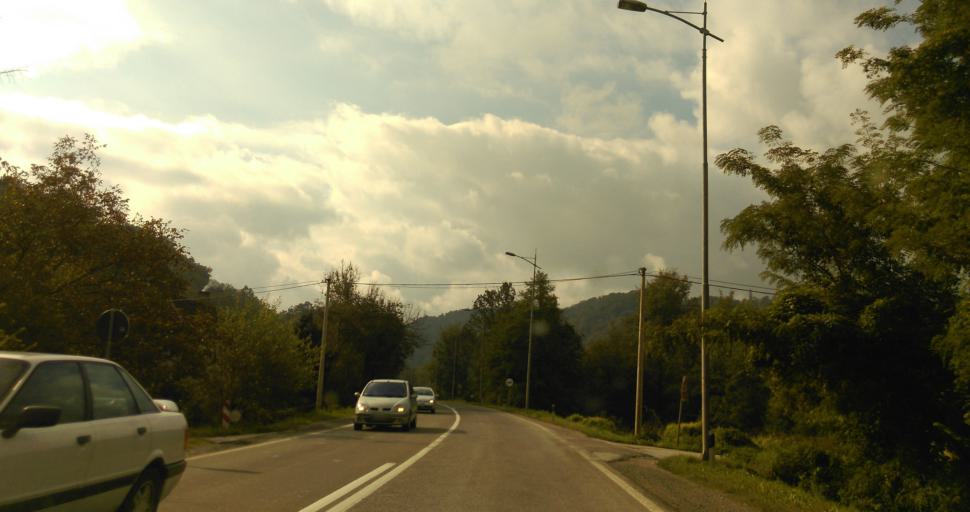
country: RS
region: Central Serbia
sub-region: Kolubarski Okrug
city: Ljig
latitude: 44.2143
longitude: 20.2268
